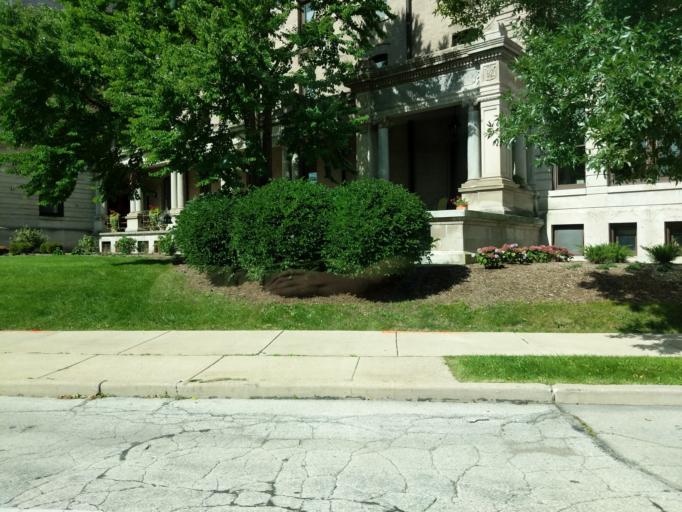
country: US
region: Wisconsin
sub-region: Milwaukee County
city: Shorewood
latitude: 43.0633
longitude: -87.8781
